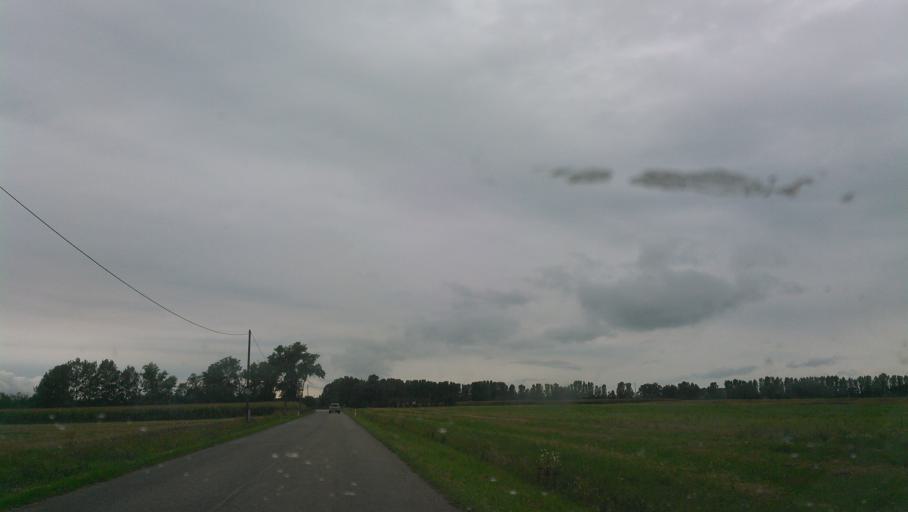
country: SK
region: Nitriansky
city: Kolarovo
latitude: 47.8807
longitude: 17.9095
